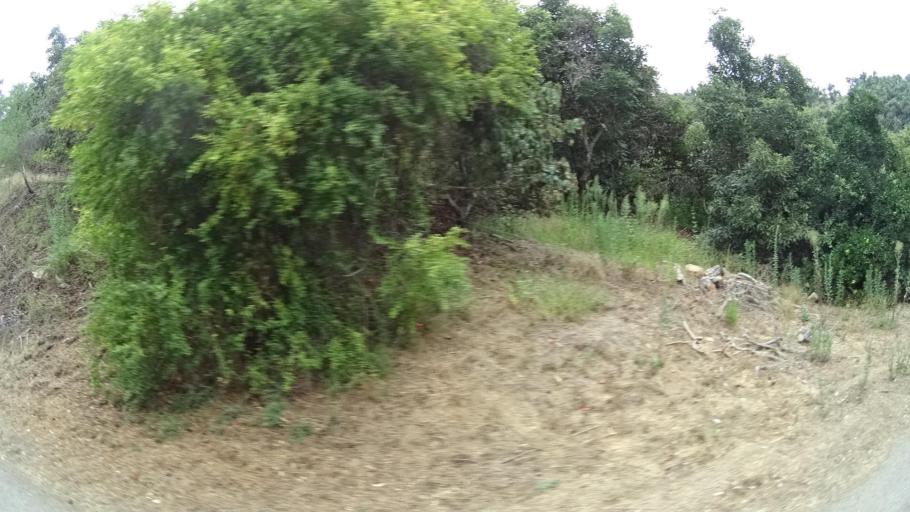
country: US
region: California
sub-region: San Diego County
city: Fallbrook
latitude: 33.4382
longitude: -117.3094
